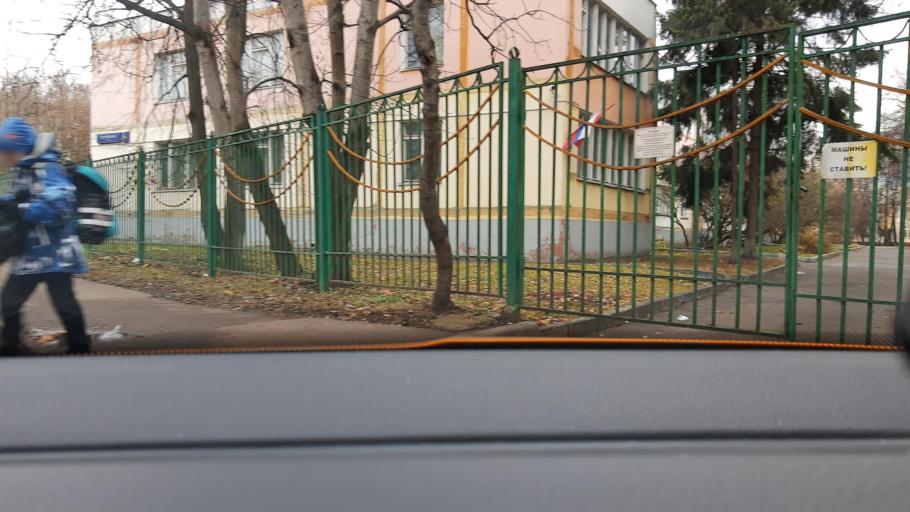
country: RU
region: Moscow
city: Gol'yanovo
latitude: 55.8061
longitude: 37.8232
